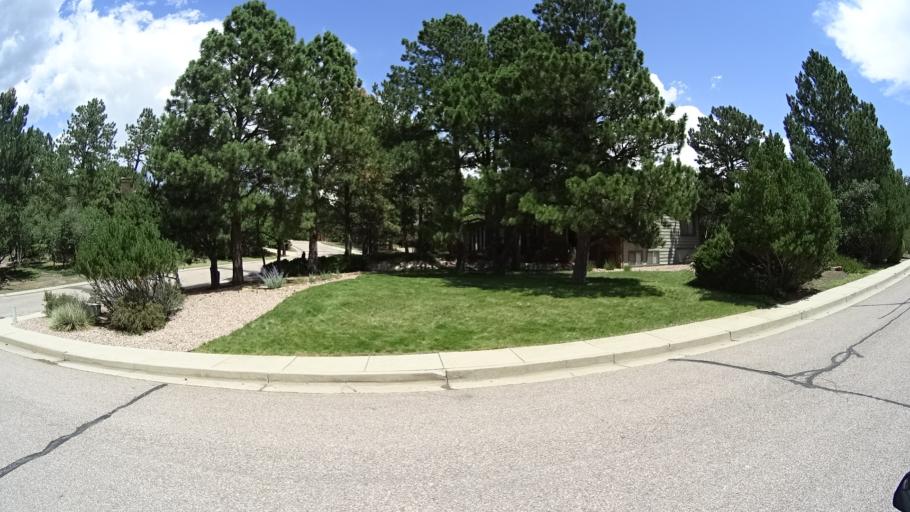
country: US
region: Colorado
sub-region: El Paso County
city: Air Force Academy
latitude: 38.9347
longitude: -104.8321
